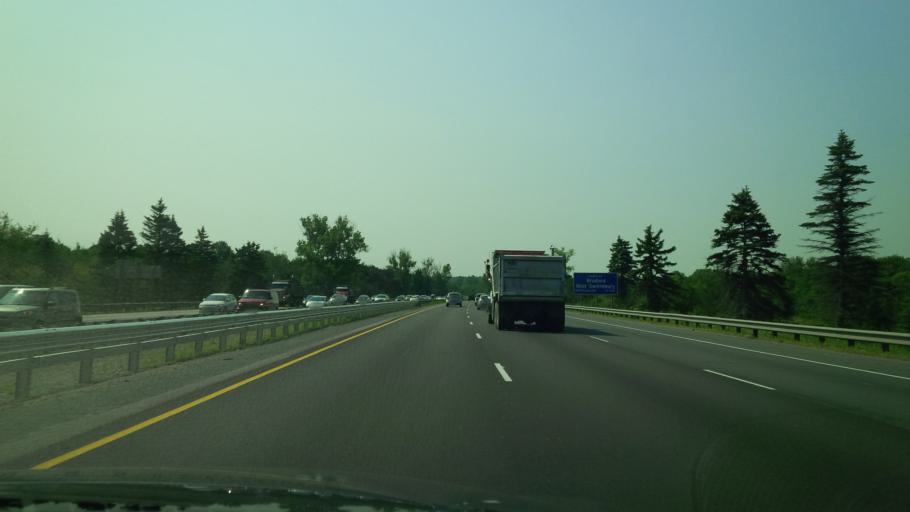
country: CA
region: Ontario
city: Bradford West Gwillimbury
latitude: 44.1829
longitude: -79.6458
